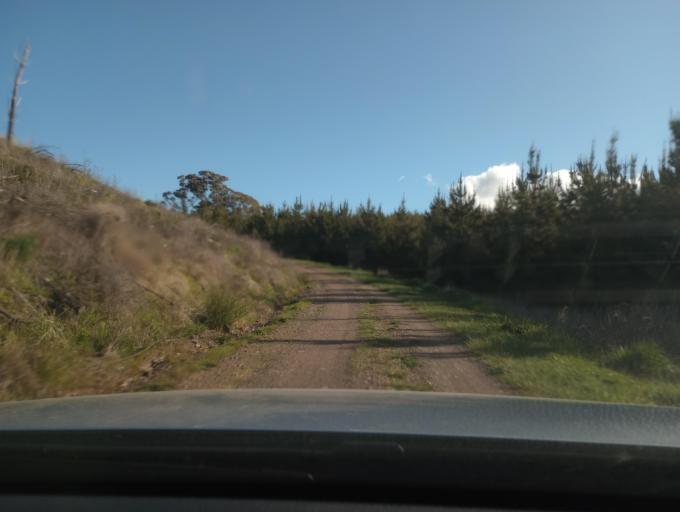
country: AU
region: New South Wales
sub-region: Blayney
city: Blayney
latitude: -33.4141
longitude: 149.3150
